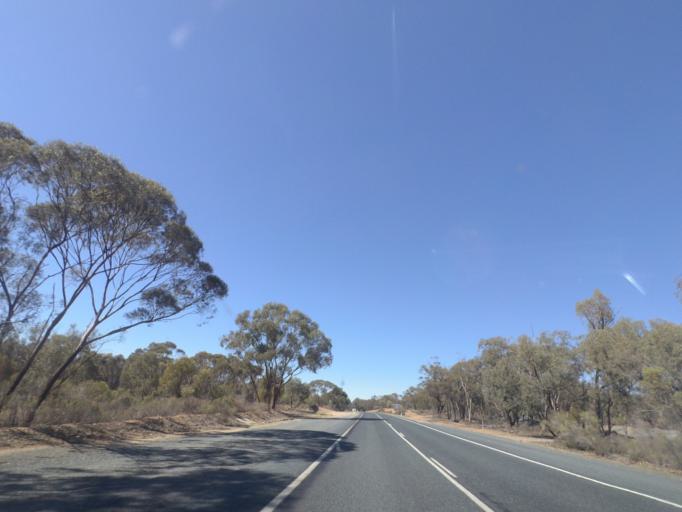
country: AU
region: New South Wales
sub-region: Bland
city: West Wyalong
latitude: -34.1371
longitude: 147.1213
